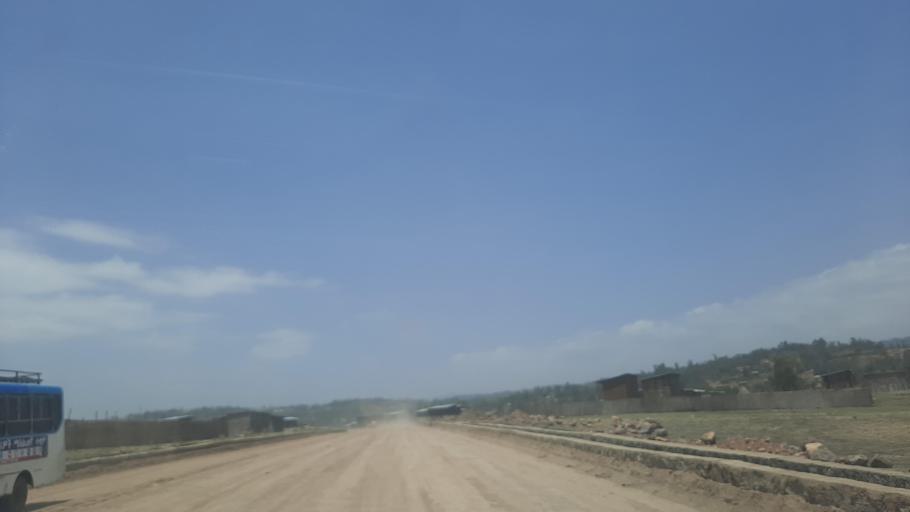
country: ET
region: Southern Nations, Nationalities, and People's Region
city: Butajira
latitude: 7.8451
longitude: 38.1745
